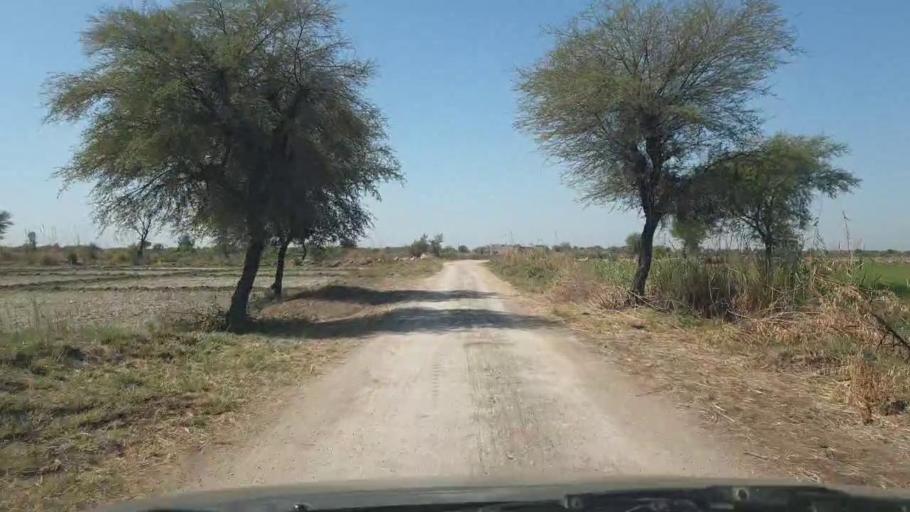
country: PK
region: Sindh
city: Dhoro Naro
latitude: 25.4492
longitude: 69.6149
